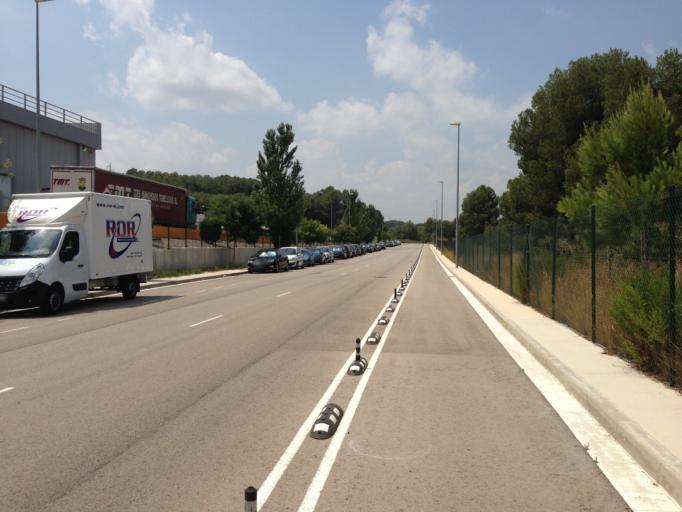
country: ES
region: Catalonia
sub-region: Provincia de Barcelona
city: Abrera
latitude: 41.5144
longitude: 1.8888
